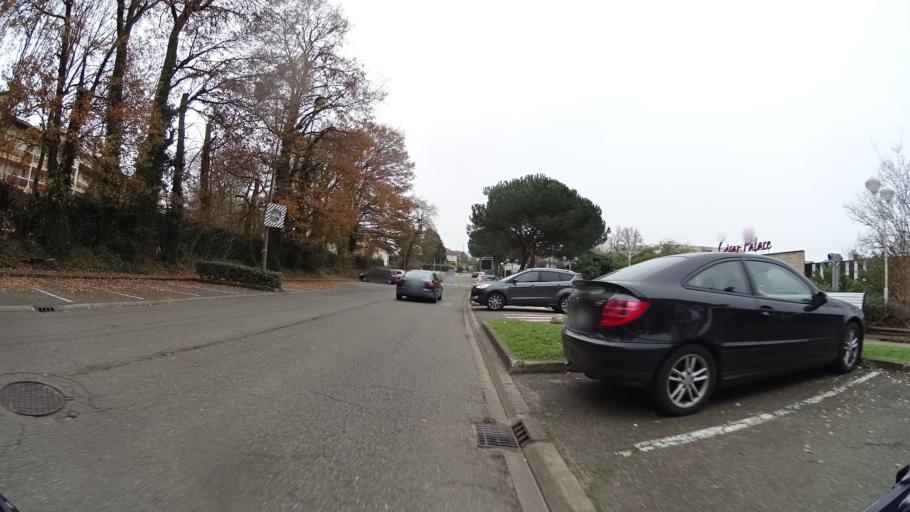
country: FR
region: Aquitaine
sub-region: Departement des Landes
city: Saint-Paul-les-Dax
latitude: 43.7266
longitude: -1.0634
